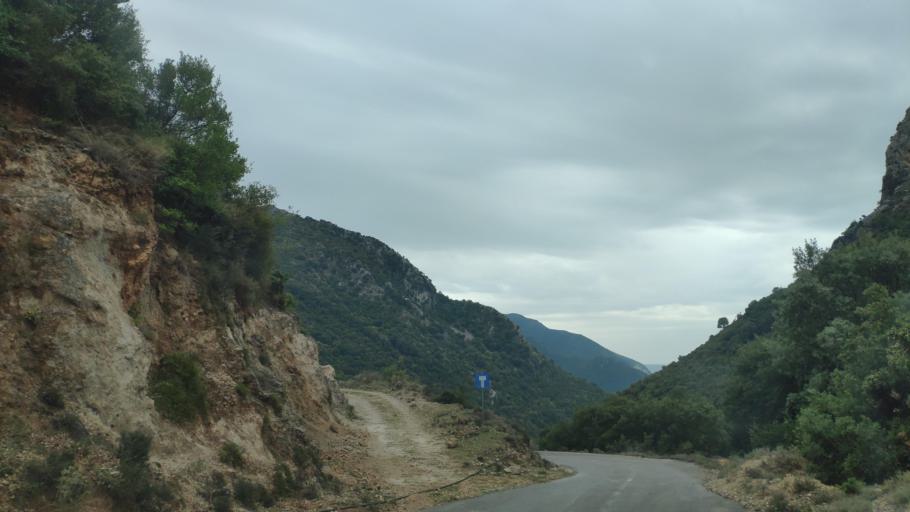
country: GR
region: Epirus
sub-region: Nomos Prevezis
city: Kanalaki
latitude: 39.3492
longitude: 20.6488
